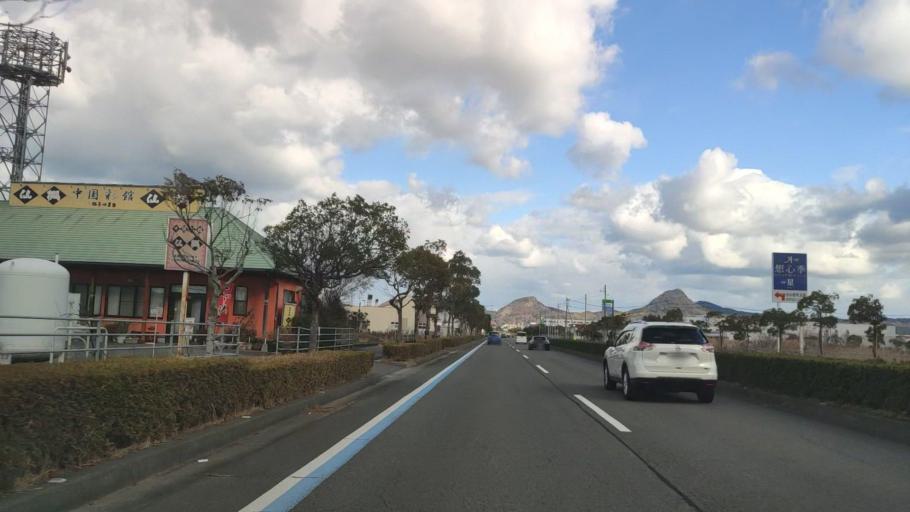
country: JP
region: Ehime
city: Hojo
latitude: 33.9579
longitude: 132.7766
